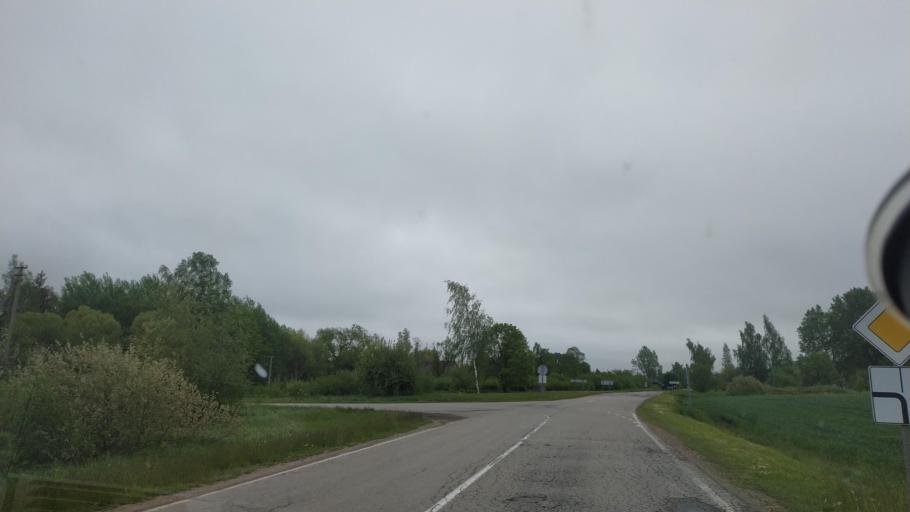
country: LT
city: Linkuva
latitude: 56.2046
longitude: 24.1255
